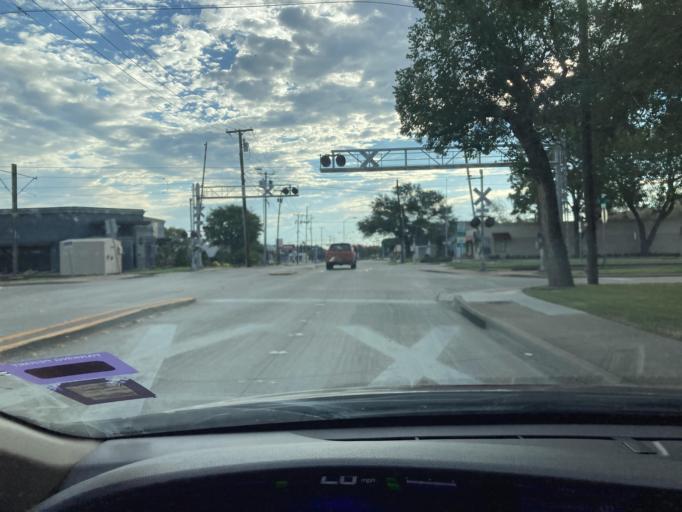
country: US
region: Texas
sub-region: Collin County
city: Plano
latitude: 33.0239
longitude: -96.7013
